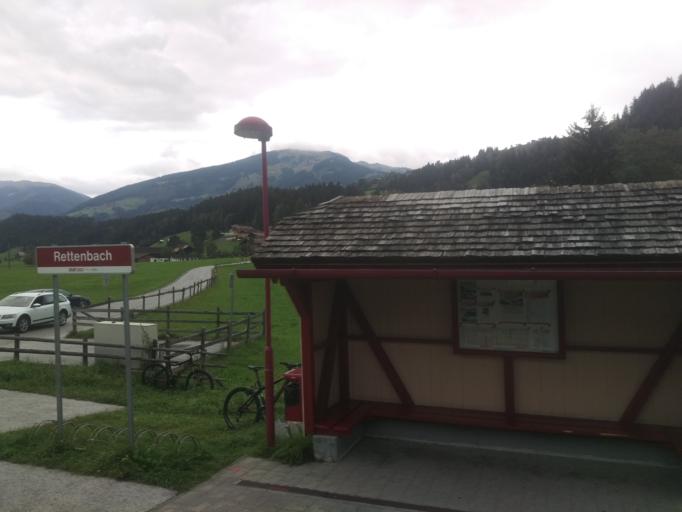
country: AT
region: Salzburg
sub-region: Politischer Bezirk Zell am See
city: Mittersill
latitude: 47.2814
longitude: 12.4498
